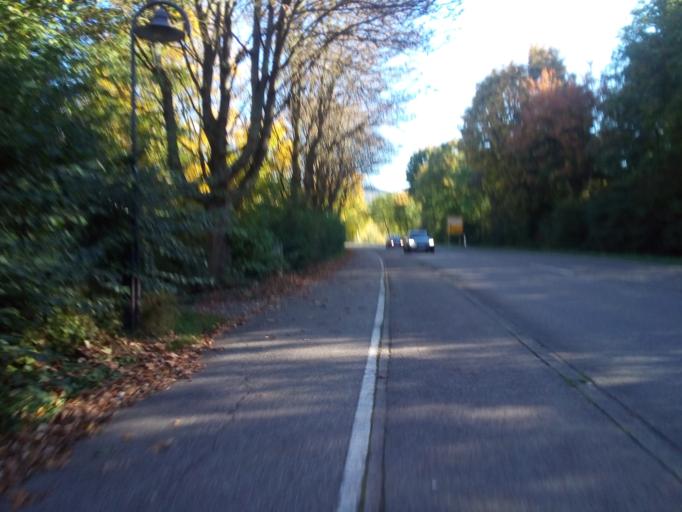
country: DE
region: Baden-Wuerttemberg
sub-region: Karlsruhe Region
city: Buhl
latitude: 48.6874
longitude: 8.1355
